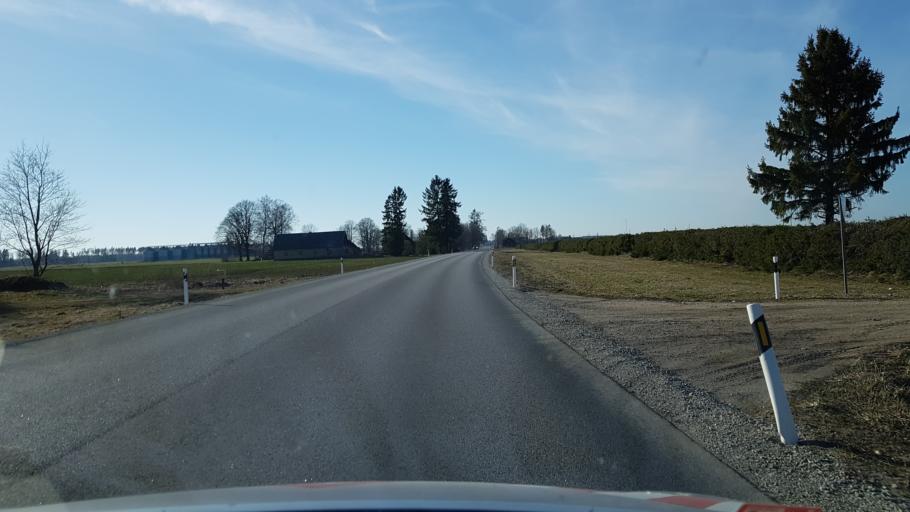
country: EE
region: Laeaene-Virumaa
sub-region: Vinni vald
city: Vinni
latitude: 59.2309
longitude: 26.5129
